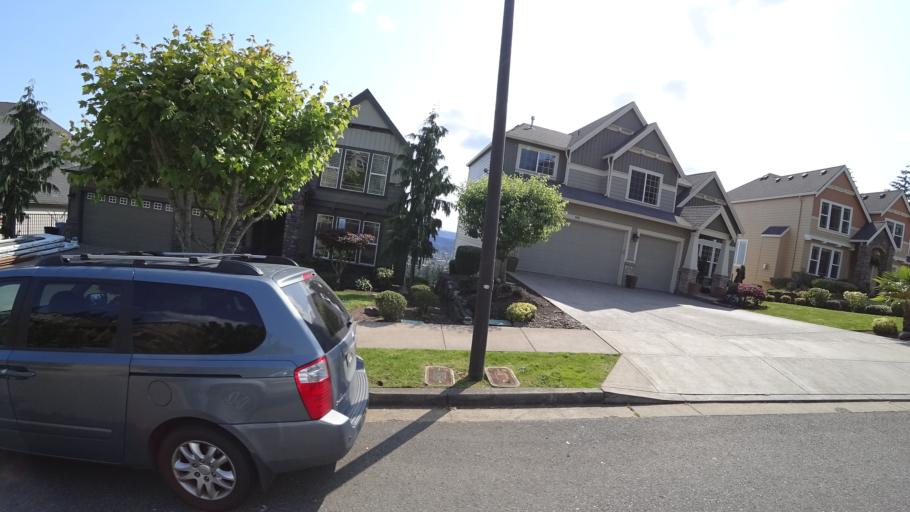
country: US
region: Oregon
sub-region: Clackamas County
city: Happy Valley
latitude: 45.4434
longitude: -122.5507
